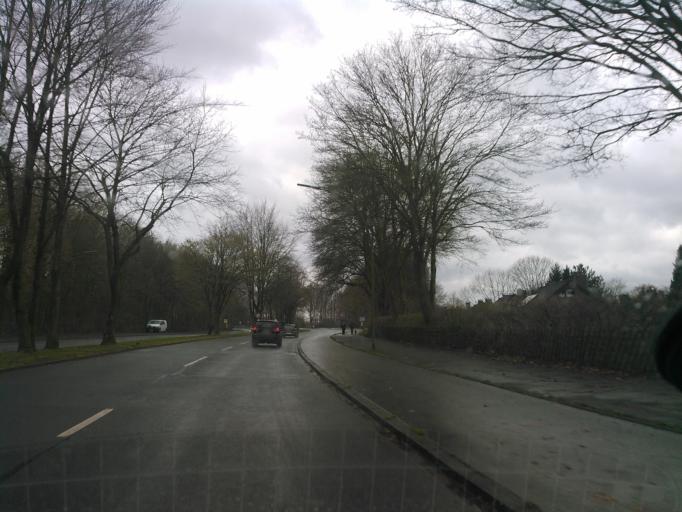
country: DE
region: North Rhine-Westphalia
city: Marl
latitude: 51.5945
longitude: 7.0635
